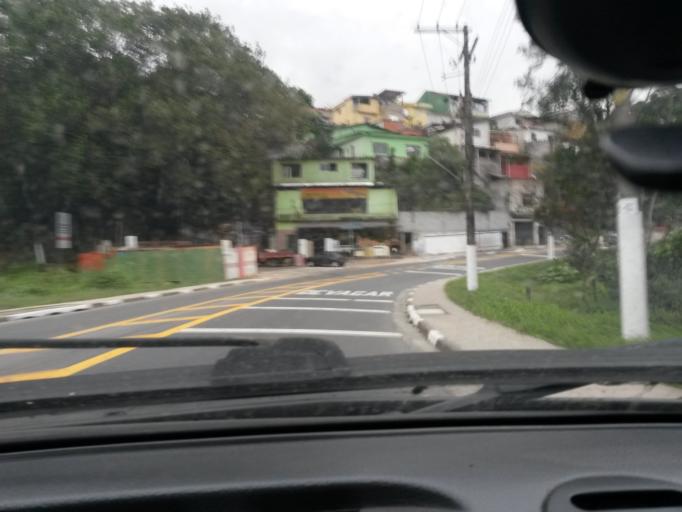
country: BR
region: Sao Paulo
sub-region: Sao Bernardo Do Campo
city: Sao Bernardo do Campo
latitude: -23.7854
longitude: -46.5314
